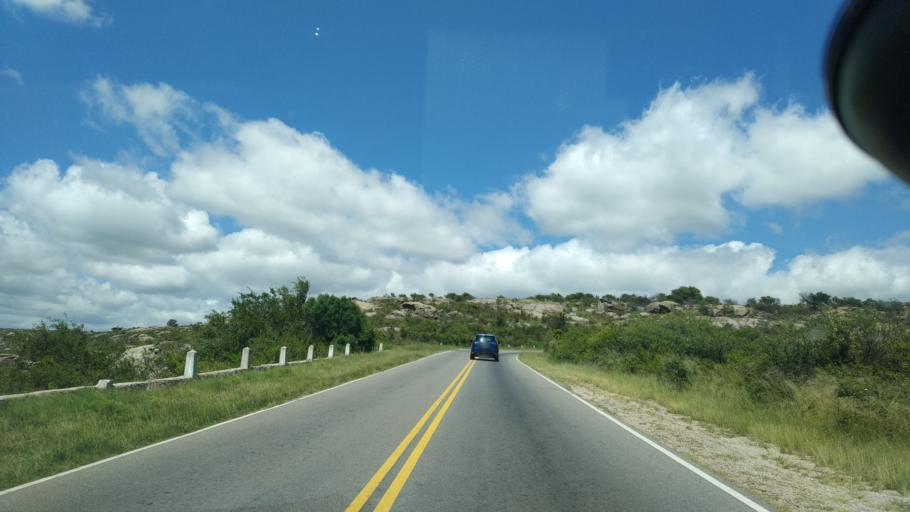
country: AR
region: Cordoba
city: Villa Cura Brochero
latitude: -31.6978
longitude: -65.0576
